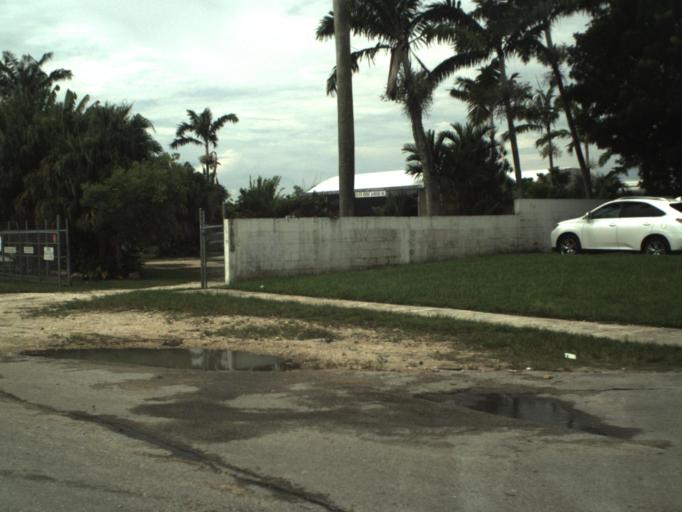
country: US
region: Florida
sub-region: Miami-Dade County
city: Naranja
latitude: 25.5501
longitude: -80.4781
